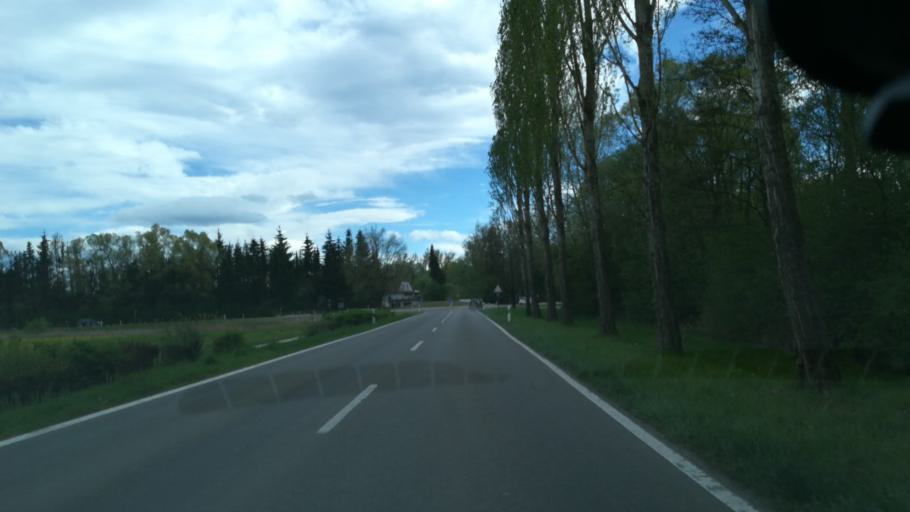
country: DE
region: Baden-Wuerttemberg
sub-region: Freiburg Region
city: Moos
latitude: 47.7438
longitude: 8.9262
